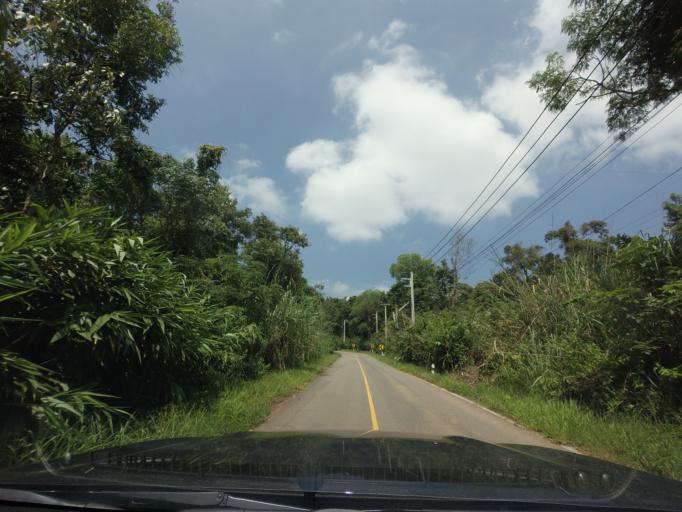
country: TH
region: Loei
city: Na Haeo
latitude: 17.4756
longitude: 100.9187
